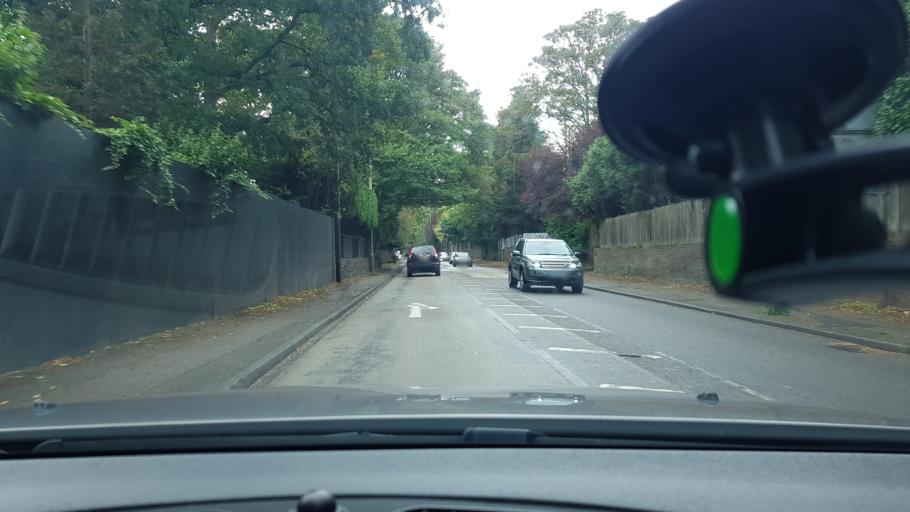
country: GB
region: England
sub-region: Hertfordshire
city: Chorleywood
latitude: 51.6548
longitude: -0.4921
